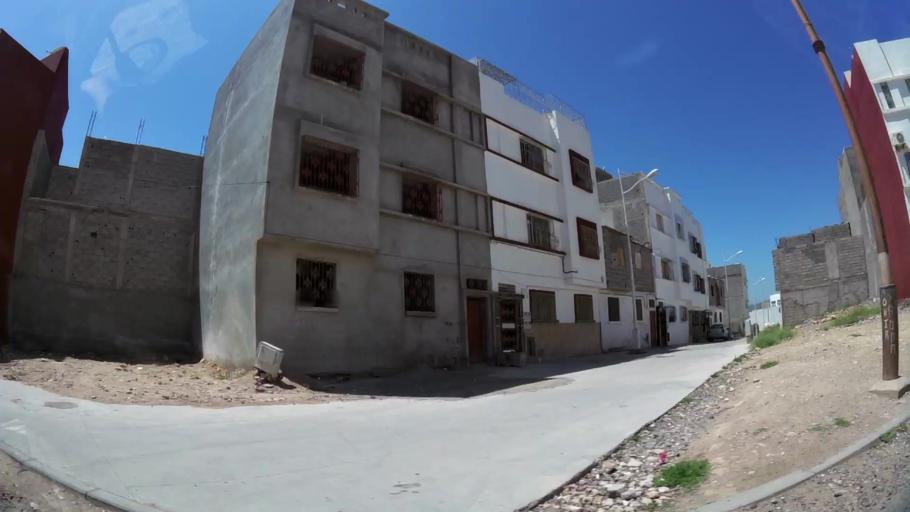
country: MA
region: Oued ed Dahab-Lagouira
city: Dakhla
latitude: 30.4443
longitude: -9.5573
